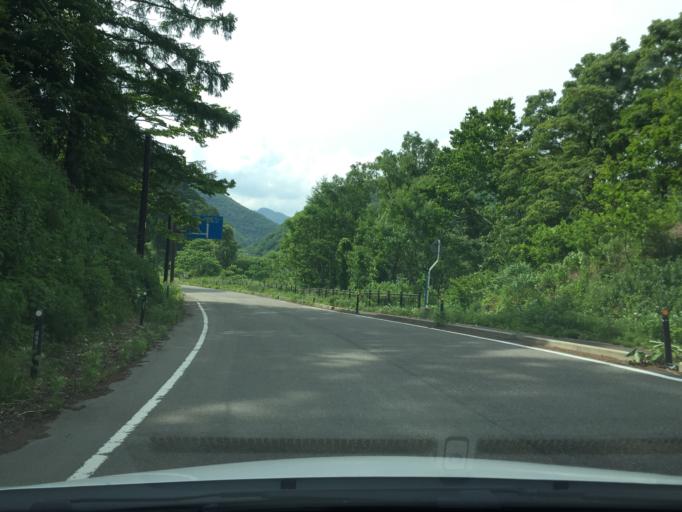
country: JP
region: Fukushima
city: Inawashiro
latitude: 37.7159
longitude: 140.0403
